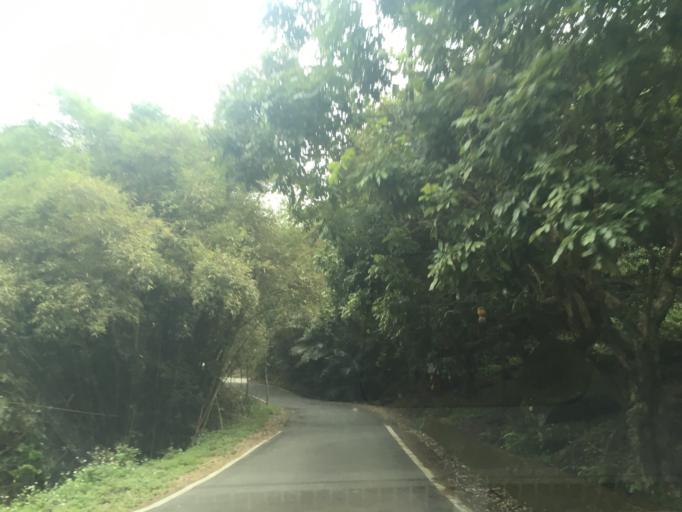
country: TW
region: Taiwan
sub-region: Taichung City
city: Taichung
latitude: 24.0583
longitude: 120.7708
